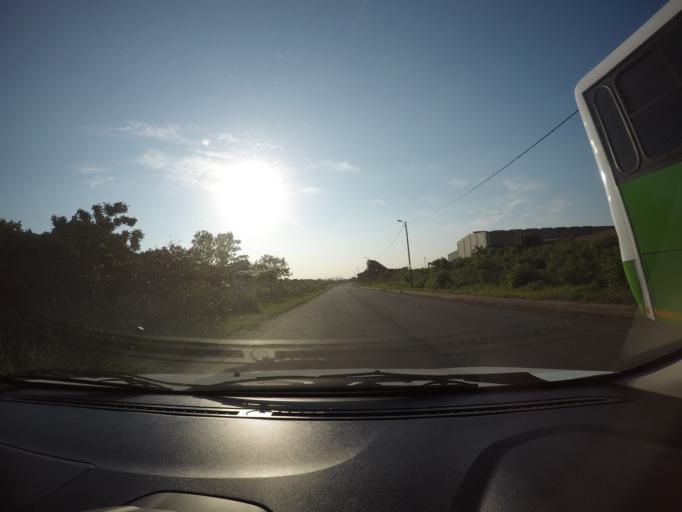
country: ZA
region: KwaZulu-Natal
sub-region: uThungulu District Municipality
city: Richards Bay
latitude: -28.7676
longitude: 32.0088
